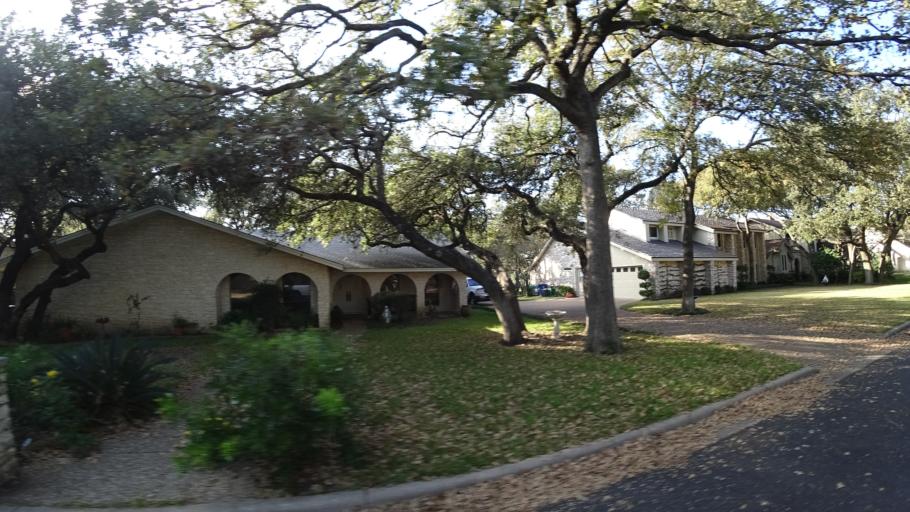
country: US
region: Texas
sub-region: Williamson County
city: Anderson Mill
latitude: 30.4323
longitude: -97.8074
